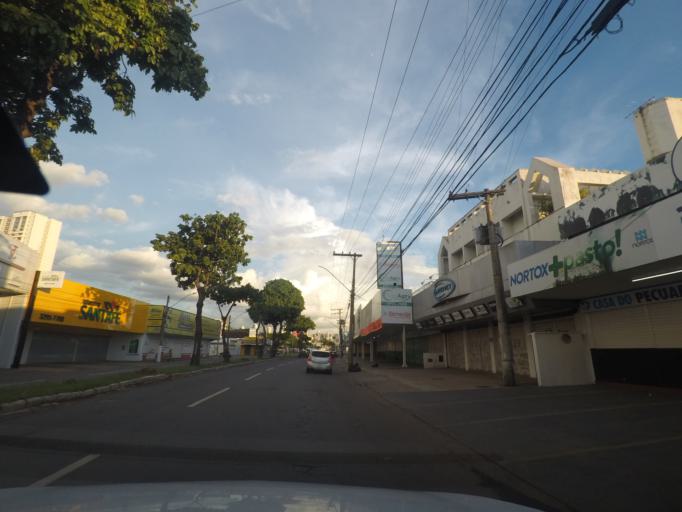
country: BR
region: Goias
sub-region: Goiania
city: Goiania
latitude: -16.6774
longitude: -49.2869
